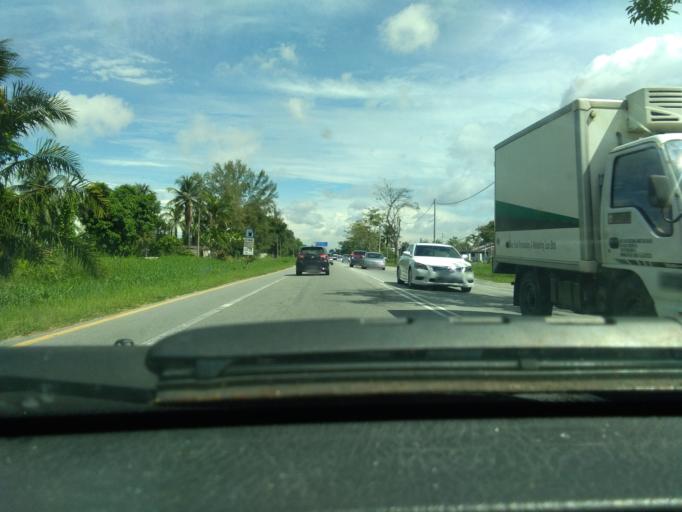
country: MY
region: Perak
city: Parit Buntar
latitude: 5.1072
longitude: 100.4842
